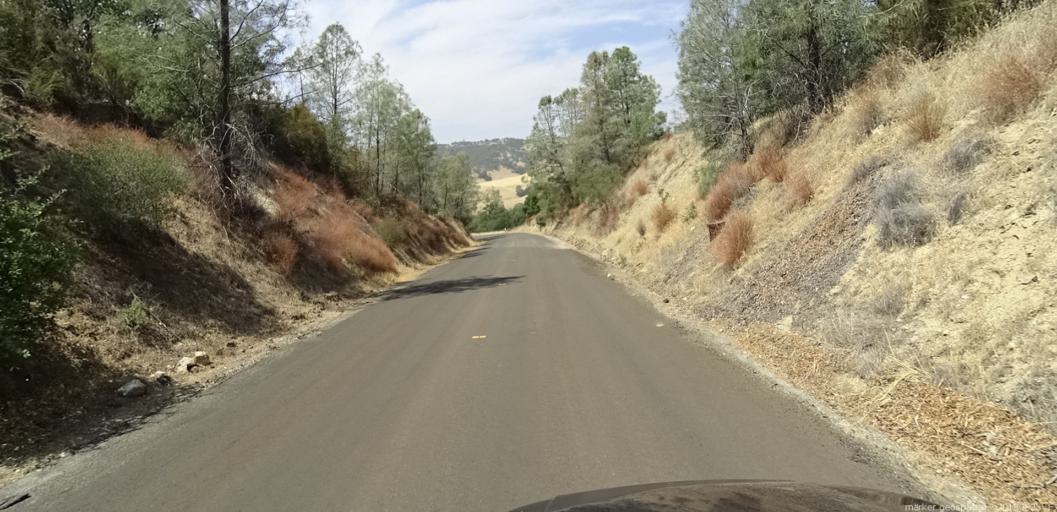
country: US
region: California
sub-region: San Luis Obispo County
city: San Miguel
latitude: 35.9098
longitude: -120.5412
